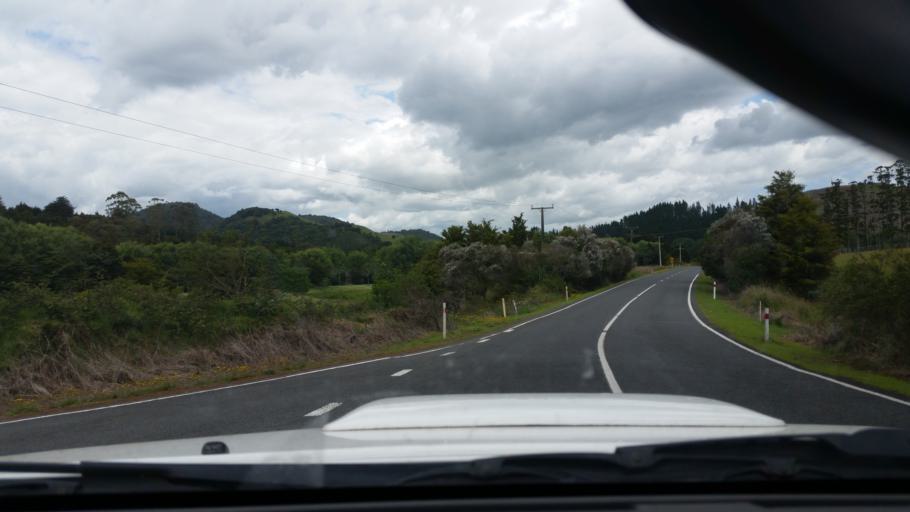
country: NZ
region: Northland
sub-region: Kaipara District
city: Dargaville
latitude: -35.7528
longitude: 173.9017
